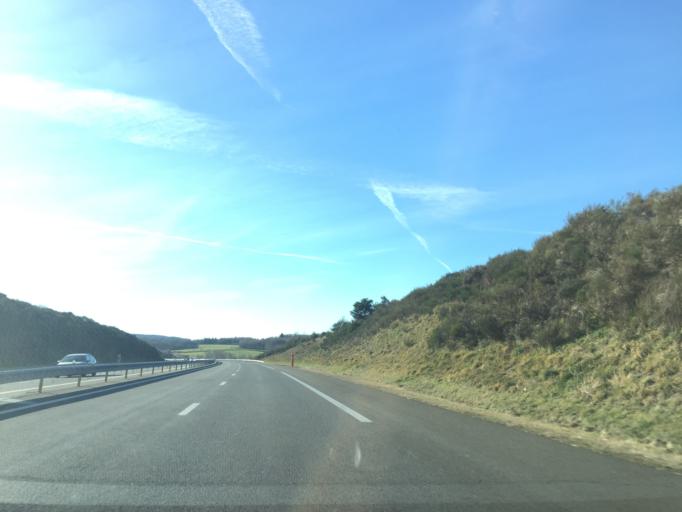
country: FR
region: Auvergne
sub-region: Departement du Puy-de-Dome
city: Gelles
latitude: 45.8198
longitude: 2.7773
